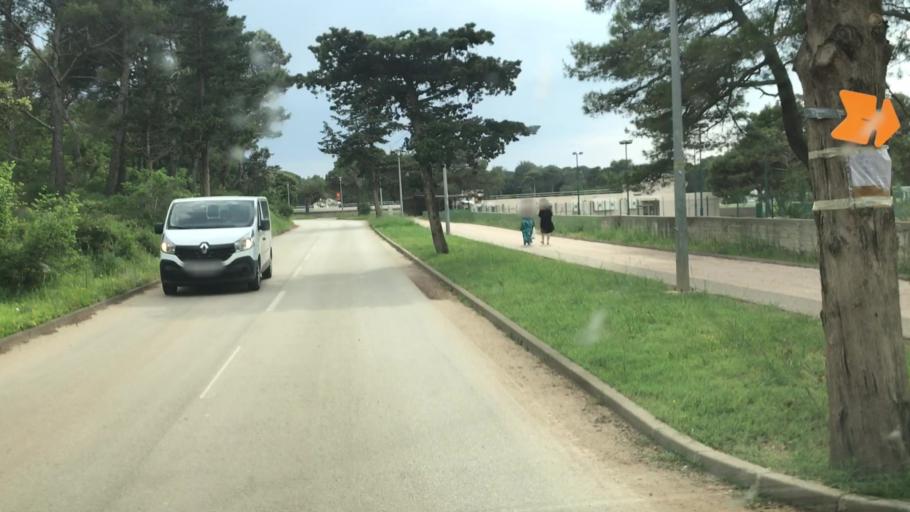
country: HR
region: Licko-Senjska
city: Novalja
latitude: 44.5473
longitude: 14.8856
